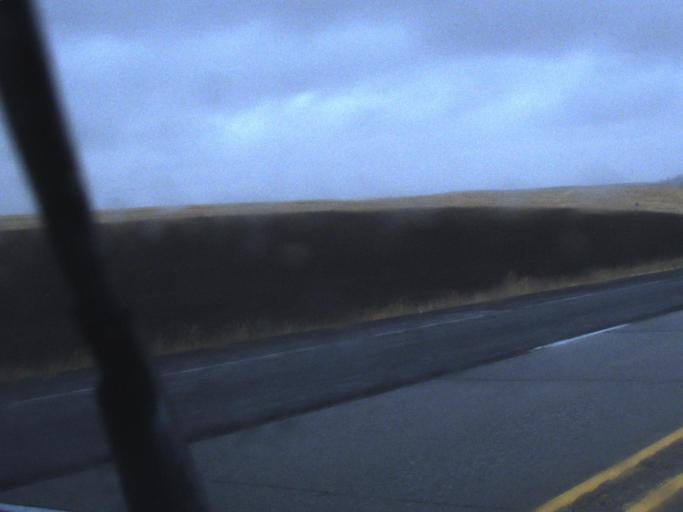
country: US
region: Washington
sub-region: Whitman County
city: Colfax
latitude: 47.2021
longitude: -117.3664
